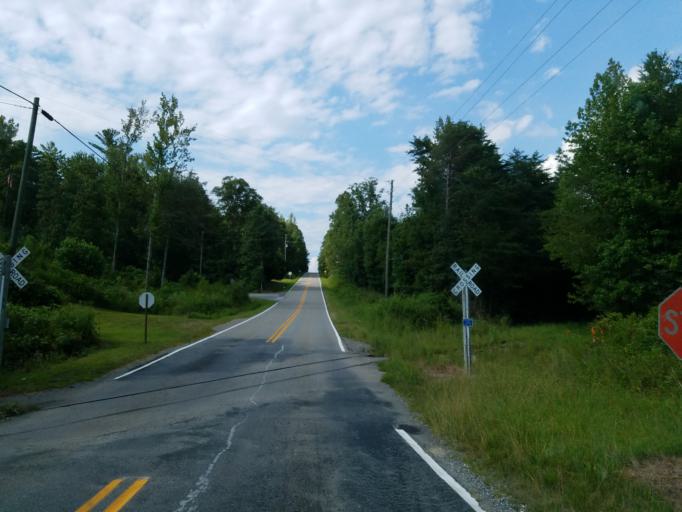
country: US
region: Georgia
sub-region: Gilmer County
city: Ellijay
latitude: 34.7426
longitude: -84.4208
